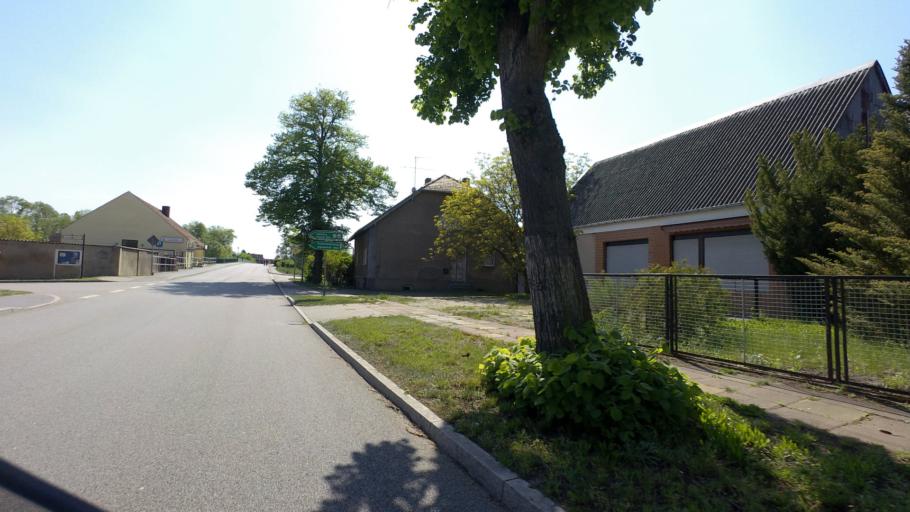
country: DE
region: Brandenburg
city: Tauche
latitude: 52.0867
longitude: 14.1713
